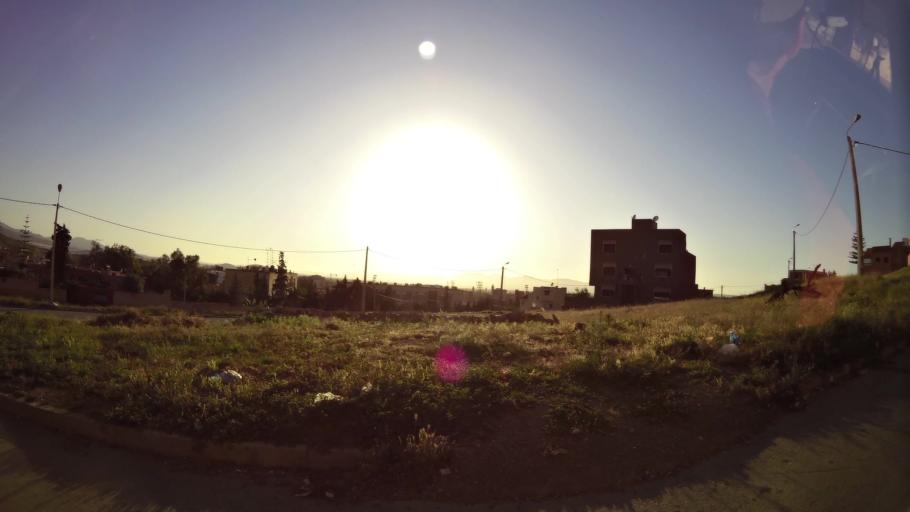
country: MA
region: Oriental
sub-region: Berkane-Taourirt
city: Berkane
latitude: 34.9262
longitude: -2.3222
